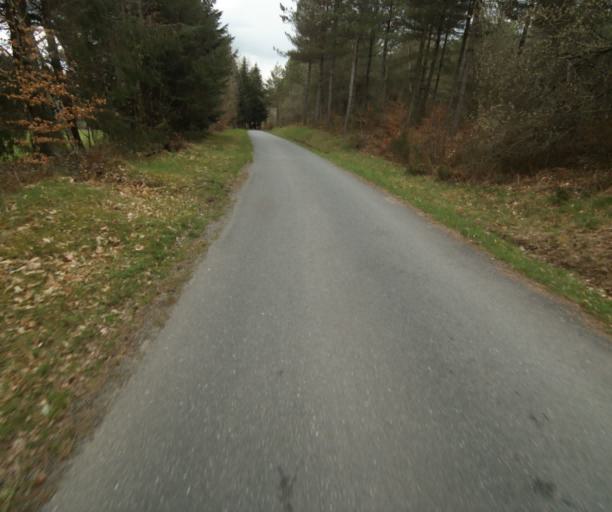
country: FR
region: Limousin
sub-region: Departement de la Correze
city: Correze
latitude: 45.3069
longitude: 1.9055
